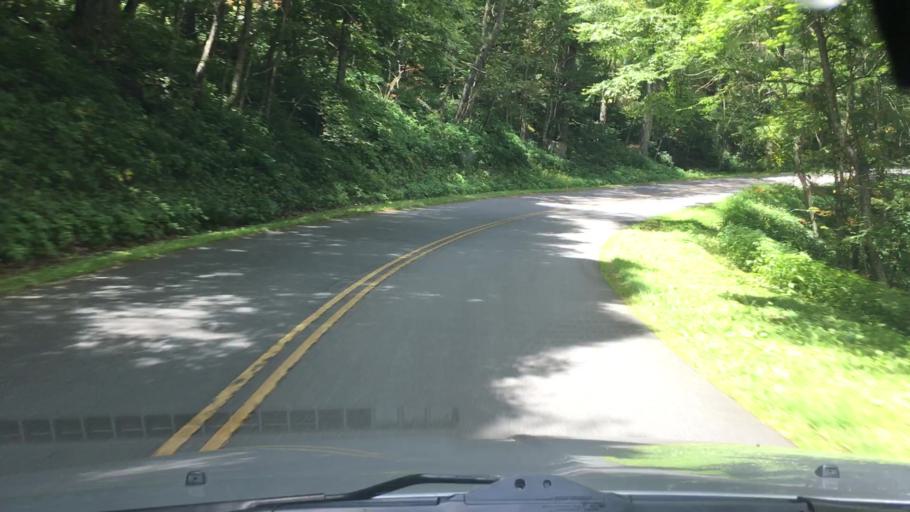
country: US
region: North Carolina
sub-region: Buncombe County
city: Swannanoa
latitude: 35.6806
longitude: -82.4175
